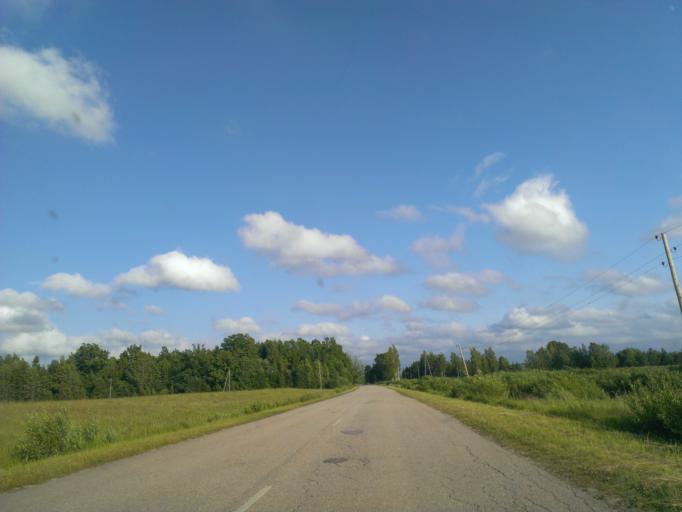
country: LV
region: Aizpute
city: Aizpute
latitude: 56.7937
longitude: 21.5052
